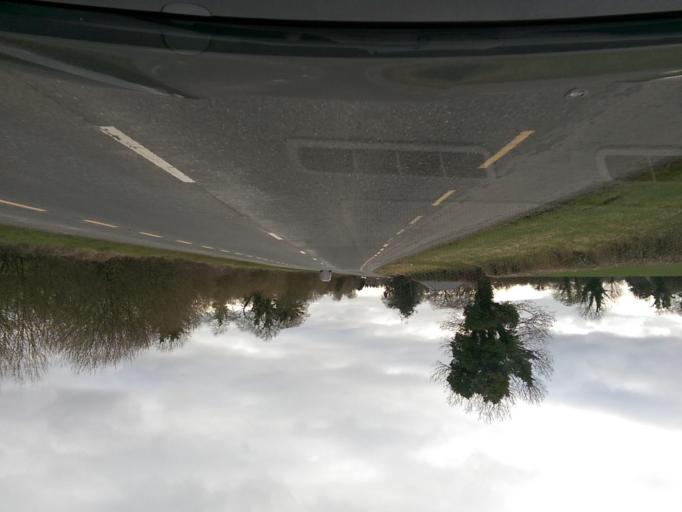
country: IE
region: Leinster
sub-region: An Iarmhi
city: Moate
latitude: 53.3914
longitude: -7.7929
